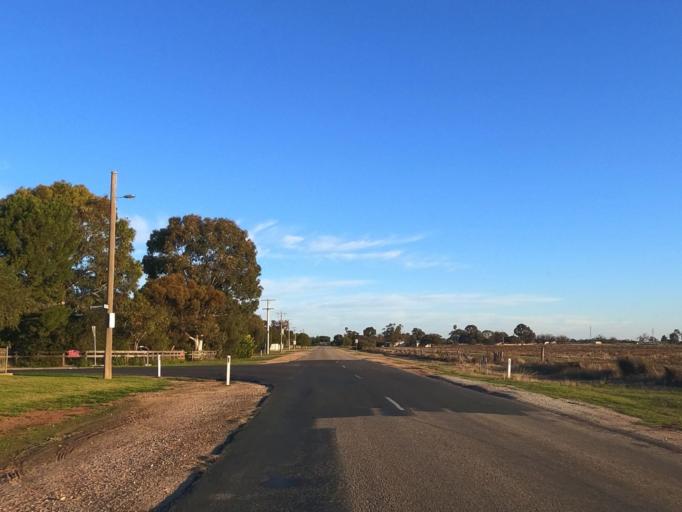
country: AU
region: Victoria
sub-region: Swan Hill
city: Swan Hill
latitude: -35.3555
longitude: 143.5526
